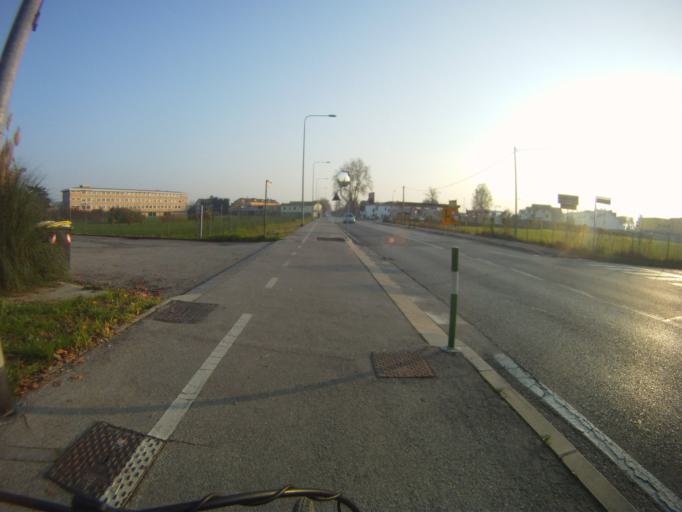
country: IT
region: Veneto
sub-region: Provincia di Padova
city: Albignasego
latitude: 45.3774
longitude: 11.8857
